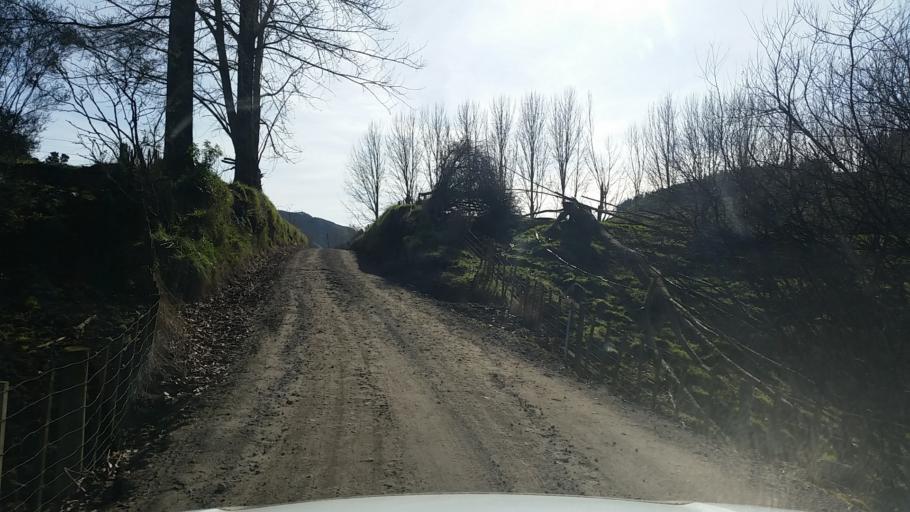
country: NZ
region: Taranaki
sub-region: South Taranaki District
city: Eltham
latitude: -39.3550
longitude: 174.5138
